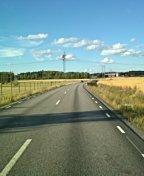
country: SE
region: Uppsala
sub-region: Habo Kommun
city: Balsta
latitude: 59.6385
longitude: 17.5245
